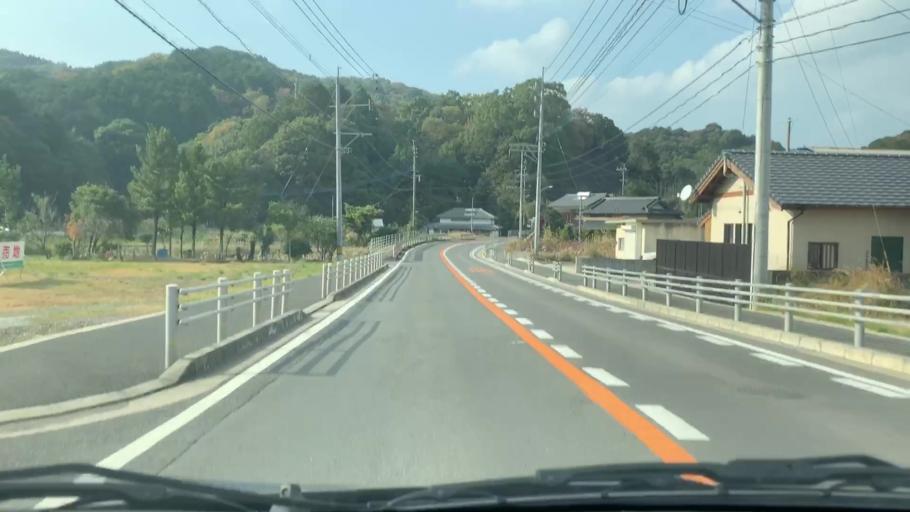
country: JP
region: Nagasaki
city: Sasebo
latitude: 32.9881
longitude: 129.7393
